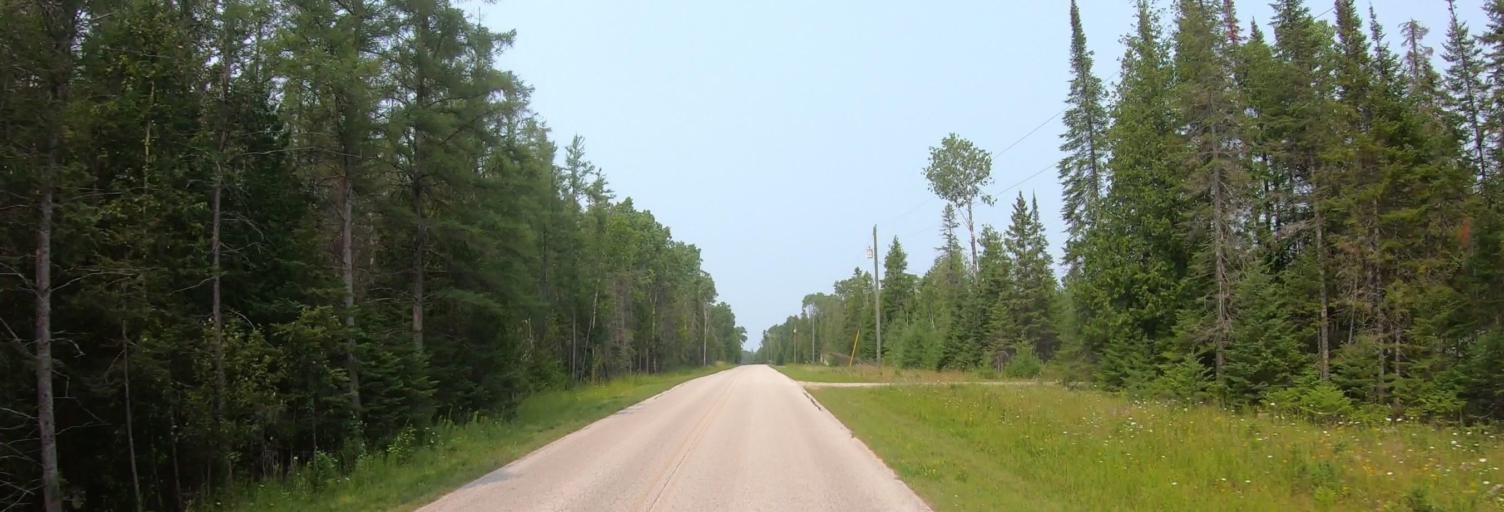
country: CA
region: Ontario
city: Thessalon
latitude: 45.9823
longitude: -83.7390
